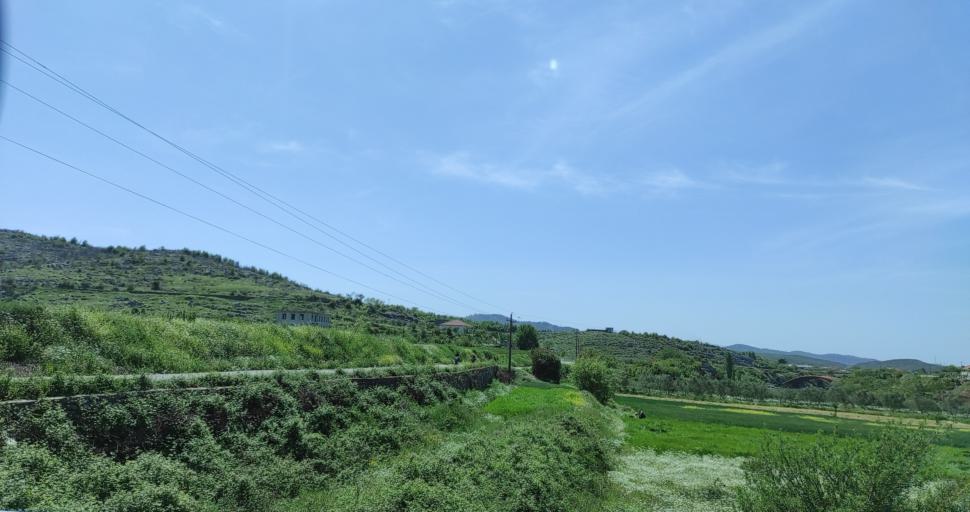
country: AL
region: Shkoder
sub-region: Rrethi i Shkodres
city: Guri i Zi
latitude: 42.1141
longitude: 19.5758
